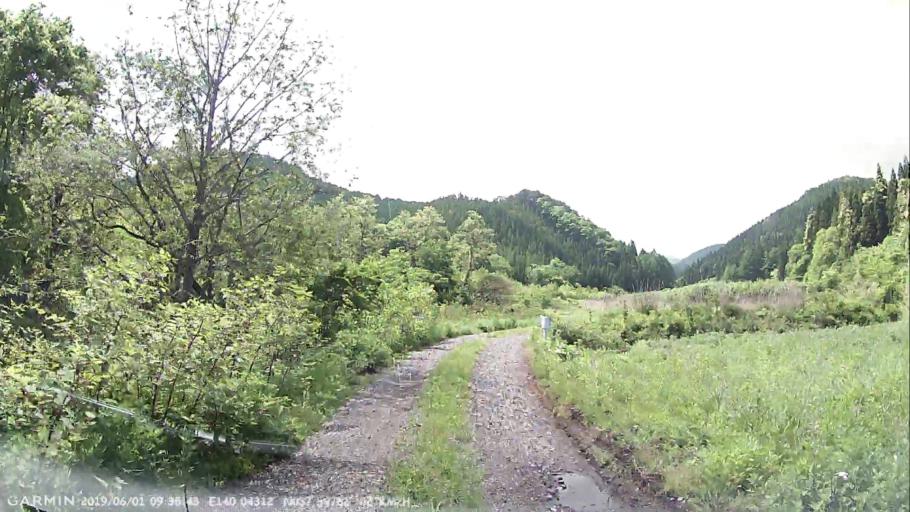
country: JP
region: Fukushima
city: Inawashiro
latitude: 37.3978
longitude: 140.0429
